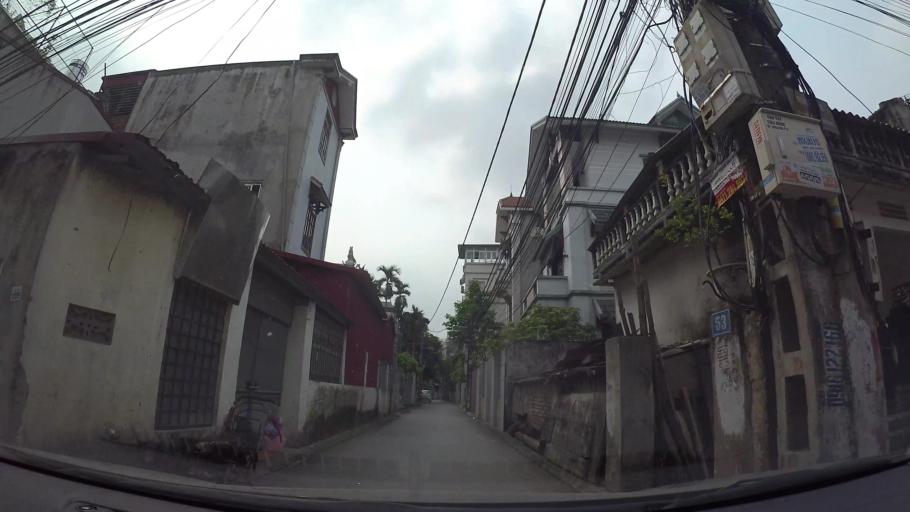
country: VN
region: Ha Noi
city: Trau Quy
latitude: 21.0524
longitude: 105.9041
